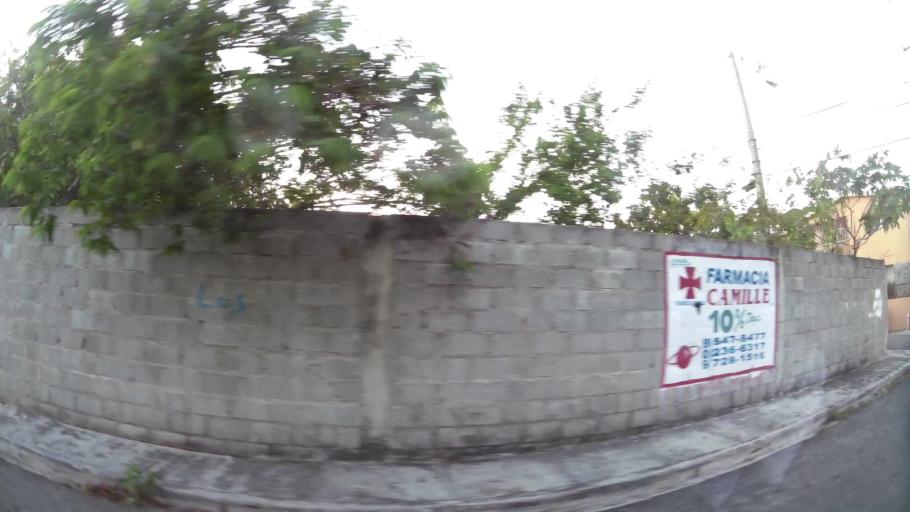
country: DO
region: Santo Domingo
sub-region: Santo Domingo
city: Santo Domingo Este
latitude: 18.4870
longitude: -69.8273
